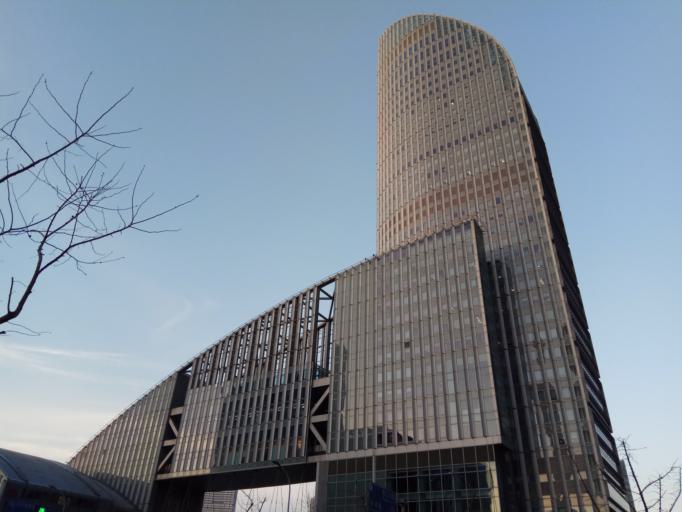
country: CN
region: Shanghai Shi
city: Hongkou
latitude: 31.2434
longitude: 121.5012
